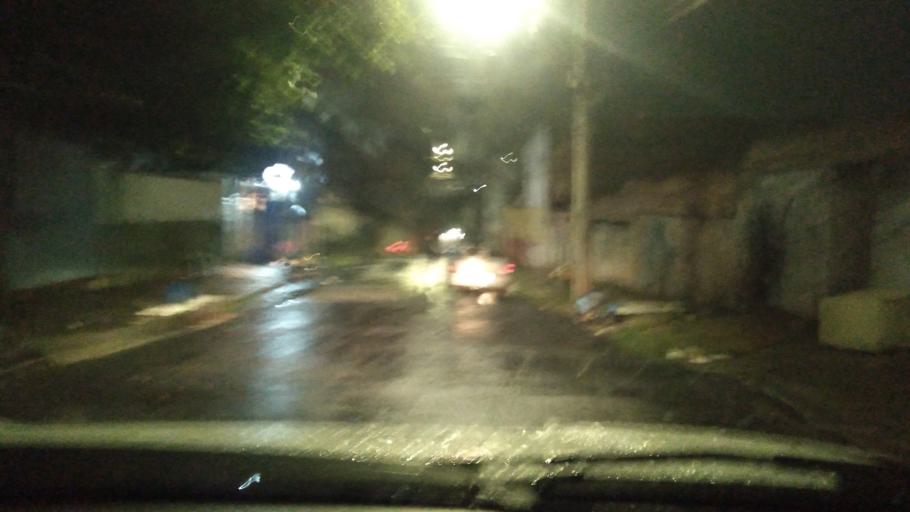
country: BR
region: Minas Gerais
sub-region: Belo Horizonte
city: Belo Horizonte
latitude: -19.9105
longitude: -43.9493
